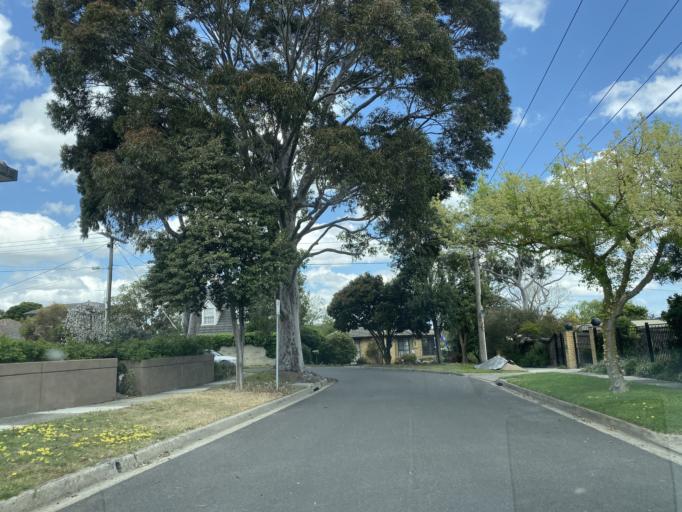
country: AU
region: Victoria
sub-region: Whitehorse
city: Burwood
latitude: -37.8591
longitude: 145.1182
